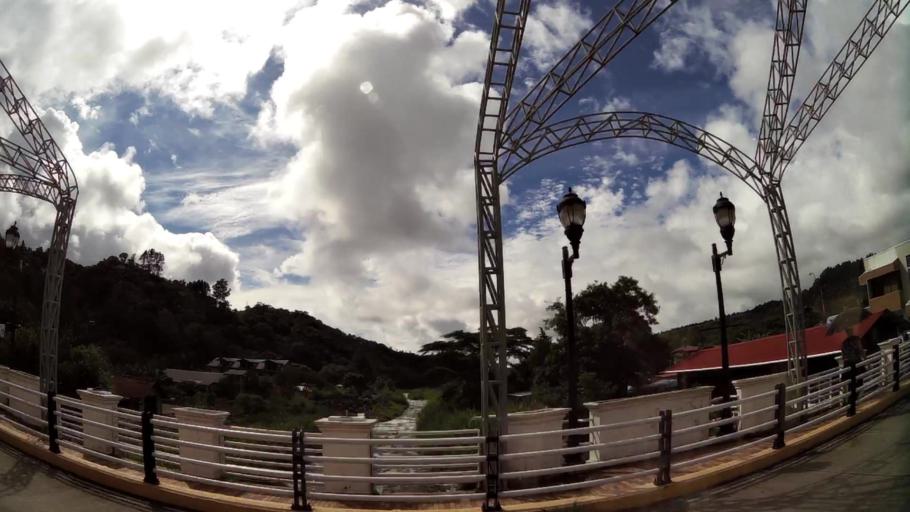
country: PA
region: Chiriqui
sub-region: Distrito Boquete
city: Boquete
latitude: 8.7763
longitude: -82.4306
